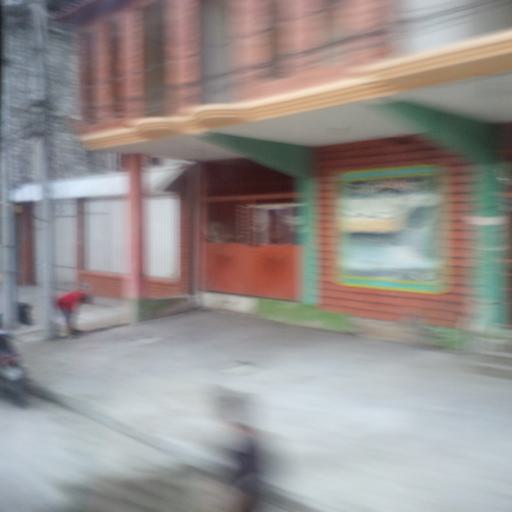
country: EC
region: Canar
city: La Troncal
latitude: -2.3327
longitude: -79.4021
